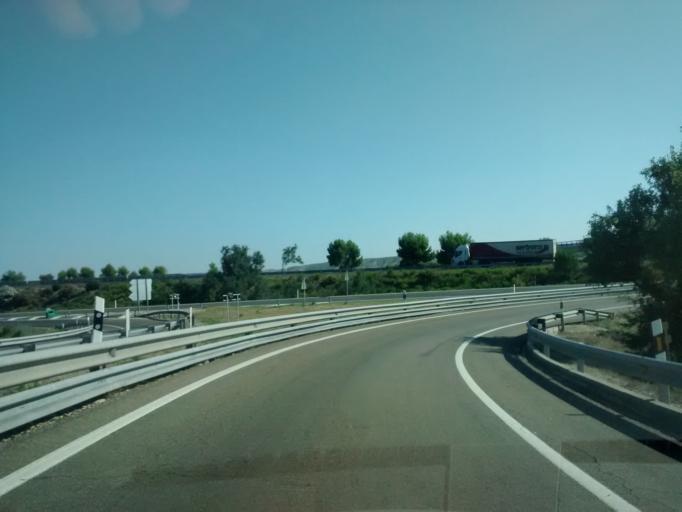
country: ES
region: Aragon
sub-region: Provincia de Zaragoza
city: Oliver-Valdefierro, Oliver, Valdefierro
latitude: 41.6754
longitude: -0.9302
